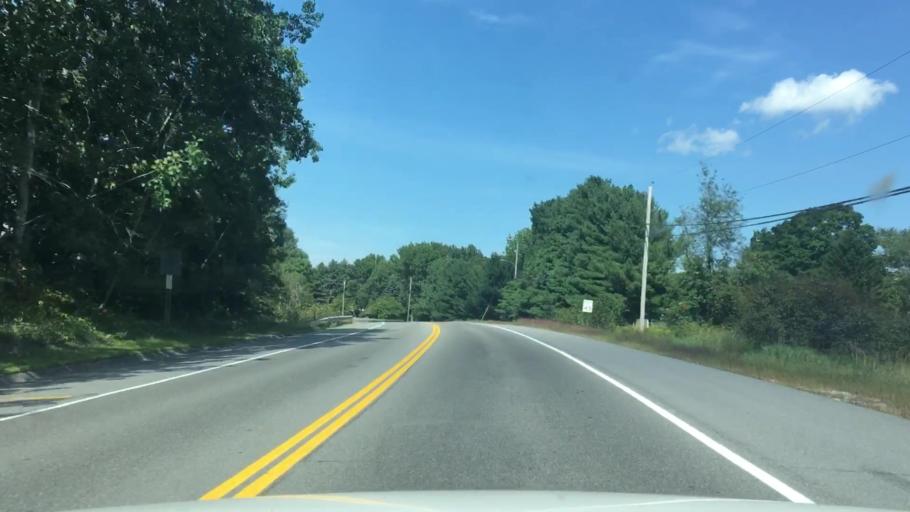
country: US
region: Maine
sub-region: Cumberland County
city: Cumberland Center
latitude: 43.7534
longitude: -70.2993
